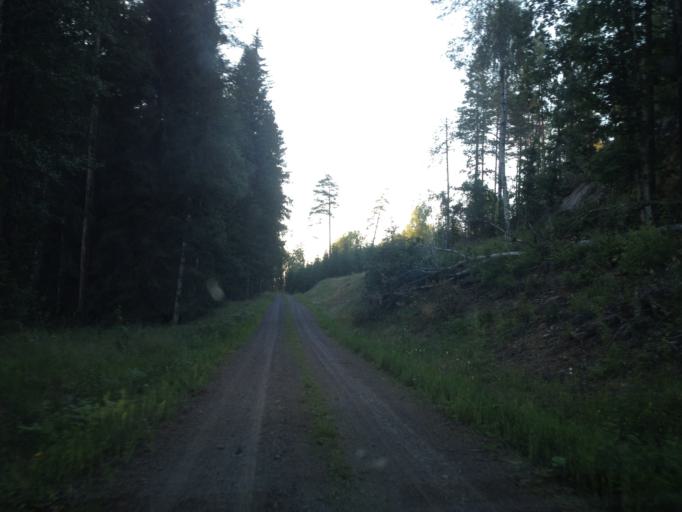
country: SE
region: Kalmar
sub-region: Vasterviks Kommun
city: Overum
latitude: 58.0098
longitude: 16.1219
